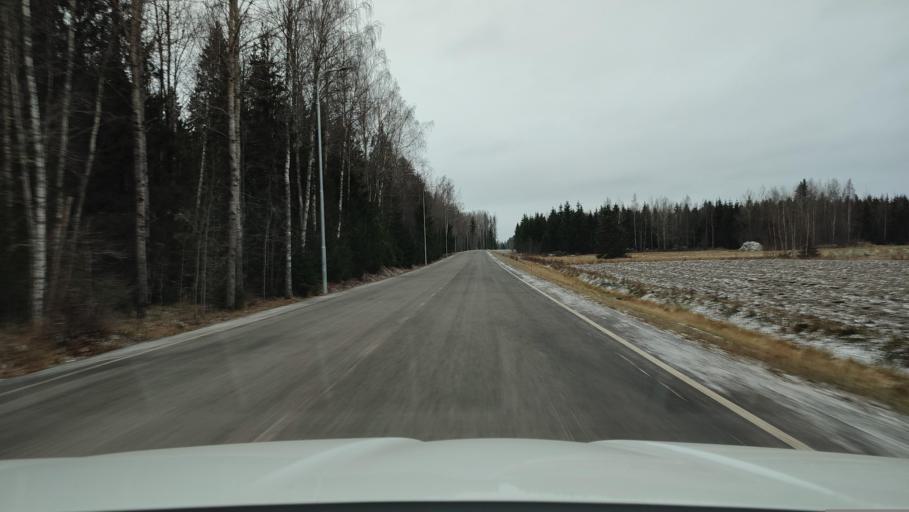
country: FI
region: Ostrobothnia
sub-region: Vaasa
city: Ristinummi
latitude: 63.0489
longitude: 21.7738
